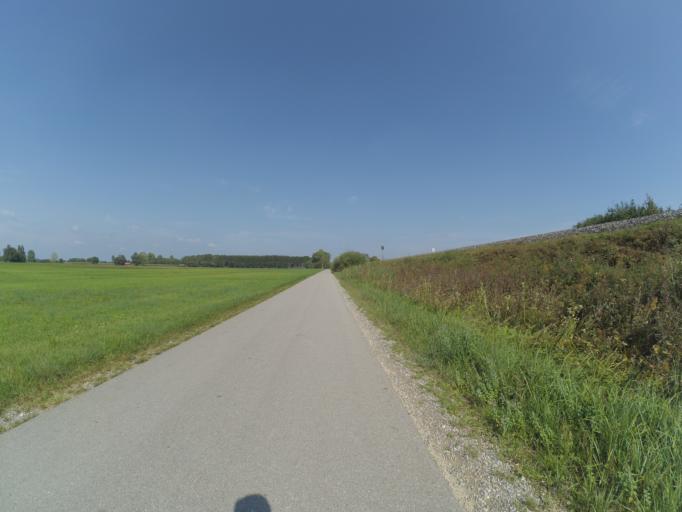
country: DE
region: Bavaria
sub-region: Swabia
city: Lamerdingen
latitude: 48.0775
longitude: 10.7296
